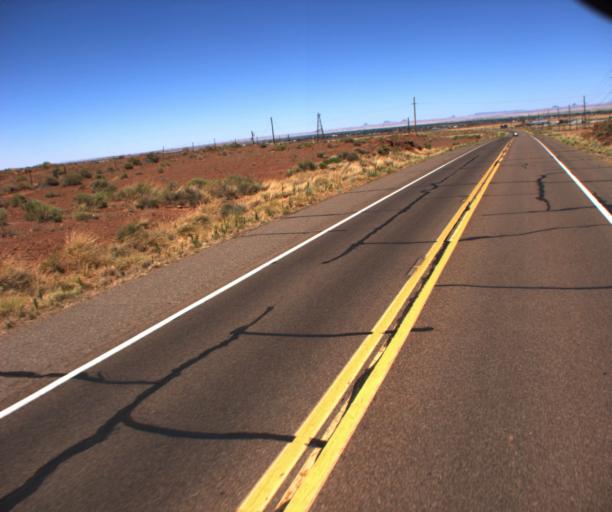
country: US
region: Arizona
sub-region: Navajo County
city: Winslow
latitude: 34.9866
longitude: -110.7132
